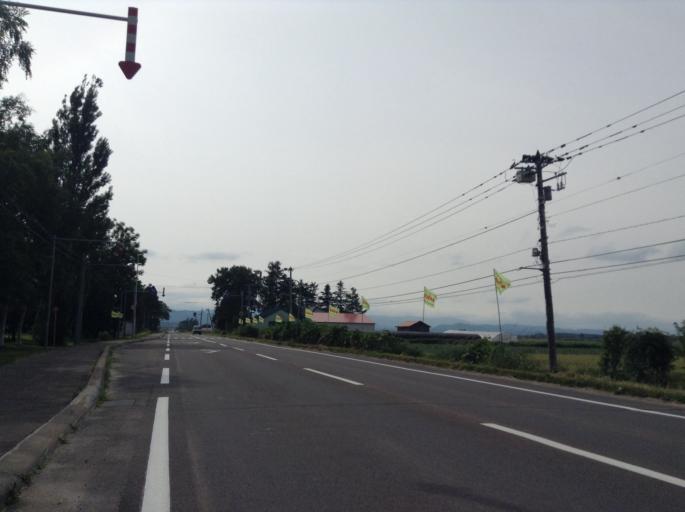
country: JP
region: Hokkaido
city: Nayoro
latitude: 44.4385
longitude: 142.3969
